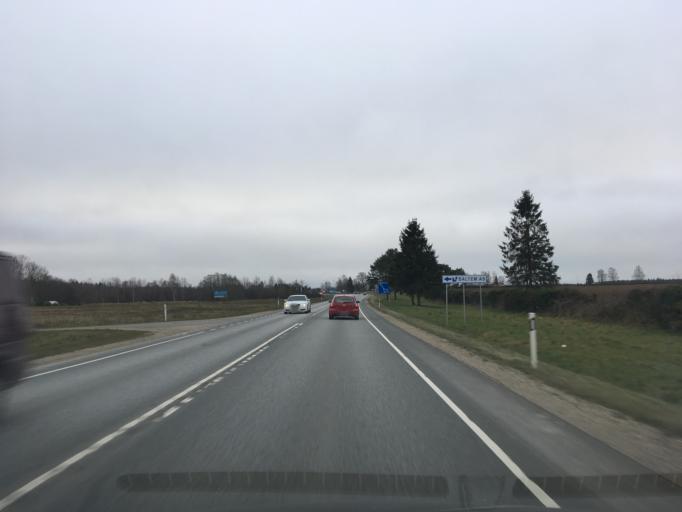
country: EE
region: Laeaene-Virumaa
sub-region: Someru vald
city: Someru
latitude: 59.3701
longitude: 26.4291
